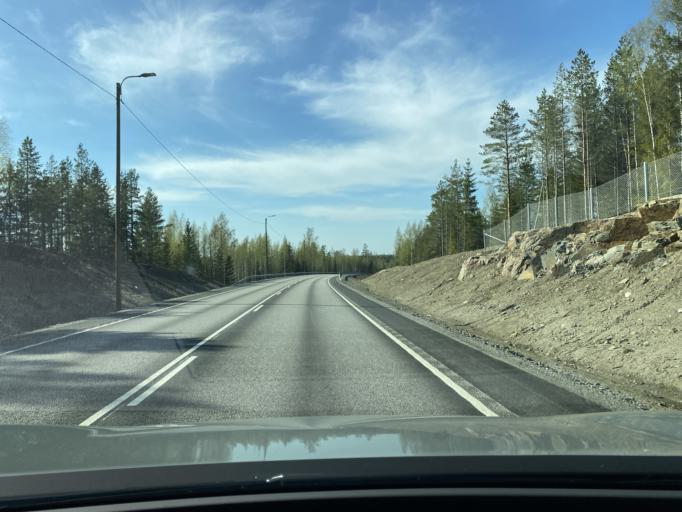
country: FI
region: Uusimaa
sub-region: Helsinki
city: Nurmijaervi
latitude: 60.4072
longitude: 24.7556
